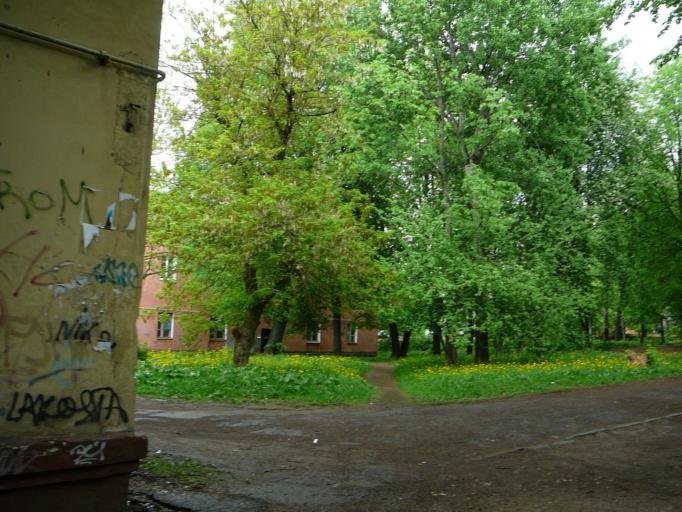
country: RU
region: Smolensk
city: Smolensk
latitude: 54.7731
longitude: 32.0339
